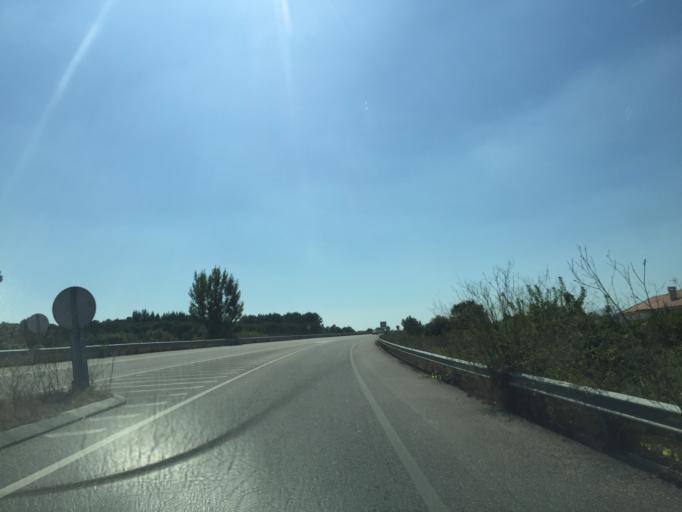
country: PT
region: Santarem
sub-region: Cartaxo
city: Pontevel
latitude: 39.1543
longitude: -8.8667
